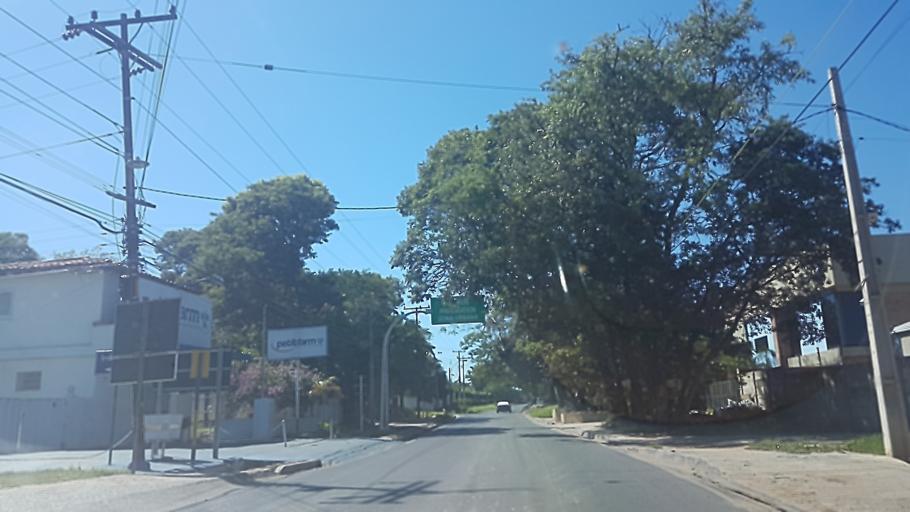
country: PY
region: Central
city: Limpio
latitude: -25.2380
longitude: -57.5092
